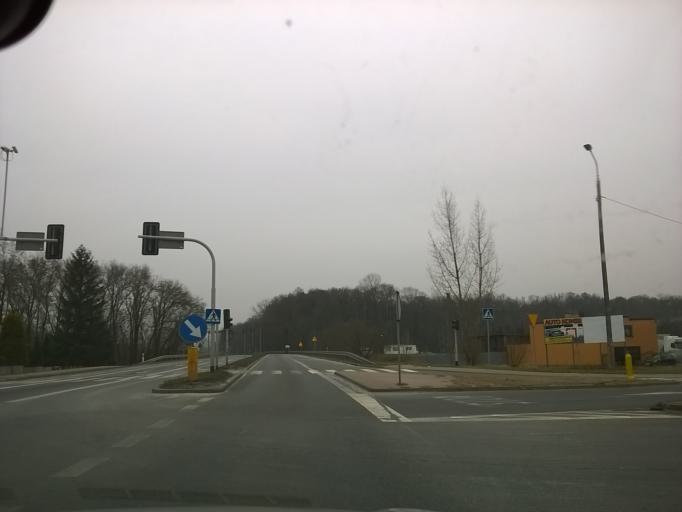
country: PL
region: Silesian Voivodeship
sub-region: Powiat gliwicki
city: Przyszowice
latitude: 50.2481
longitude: 18.7462
